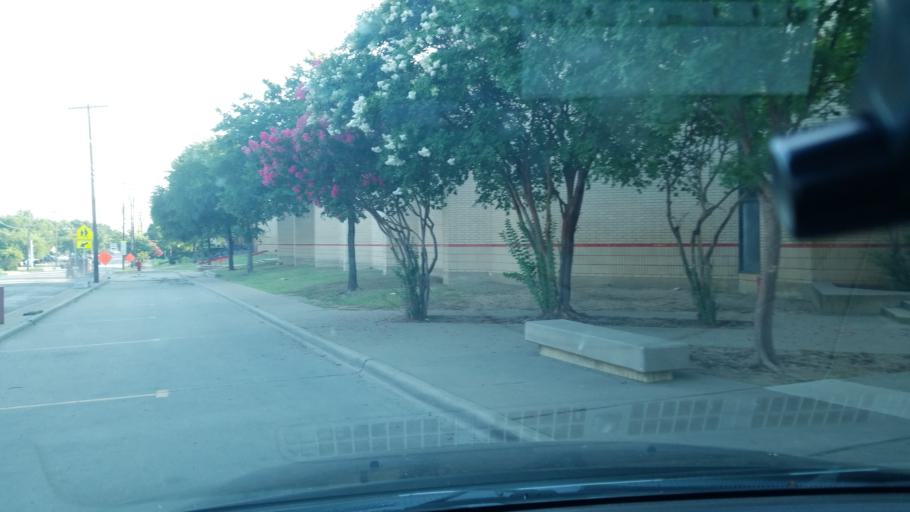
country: US
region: Texas
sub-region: Dallas County
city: Dallas
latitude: 32.7523
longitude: -96.8155
